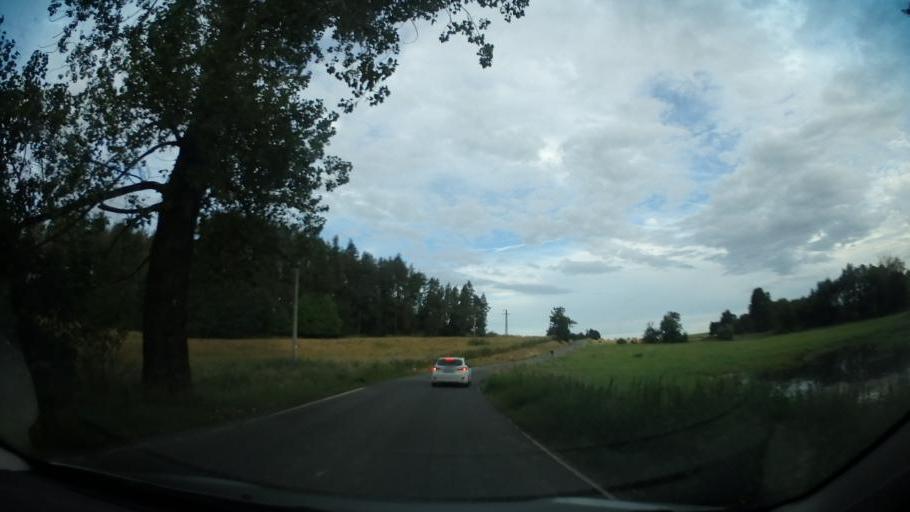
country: CZ
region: Olomoucky
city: Horni Stepanov
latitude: 49.5542
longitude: 16.7764
